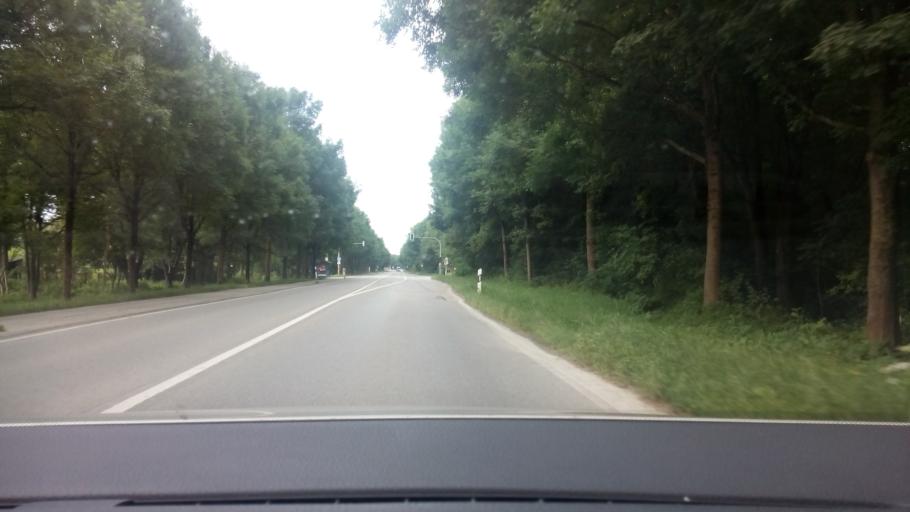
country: DE
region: Bavaria
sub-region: Upper Bavaria
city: Unterfoehring
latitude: 48.2056
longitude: 11.6303
